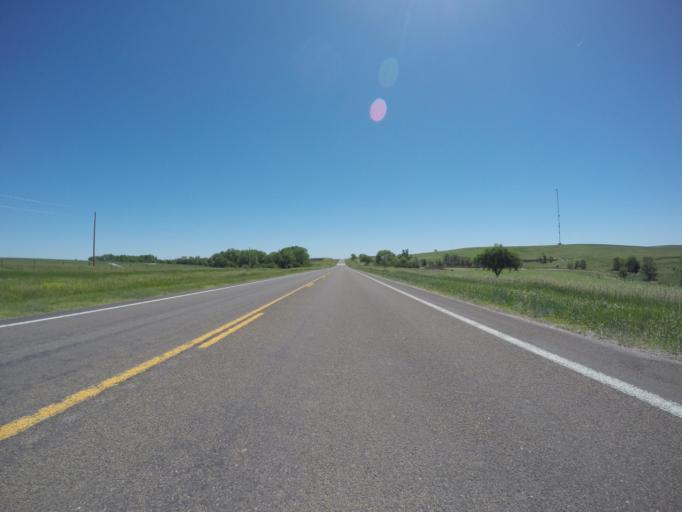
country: US
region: Kansas
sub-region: Phillips County
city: Phillipsburg
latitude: 39.8286
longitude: -99.5964
